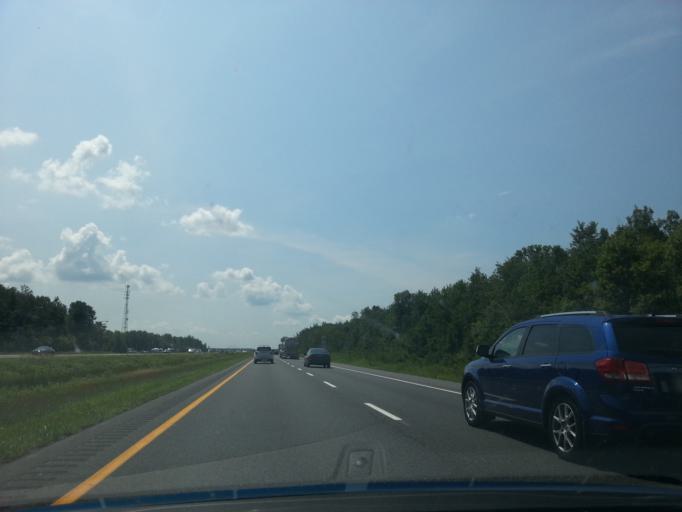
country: CA
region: Quebec
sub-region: Mauricie
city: Daveluyville
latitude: 46.1900
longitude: -72.1012
